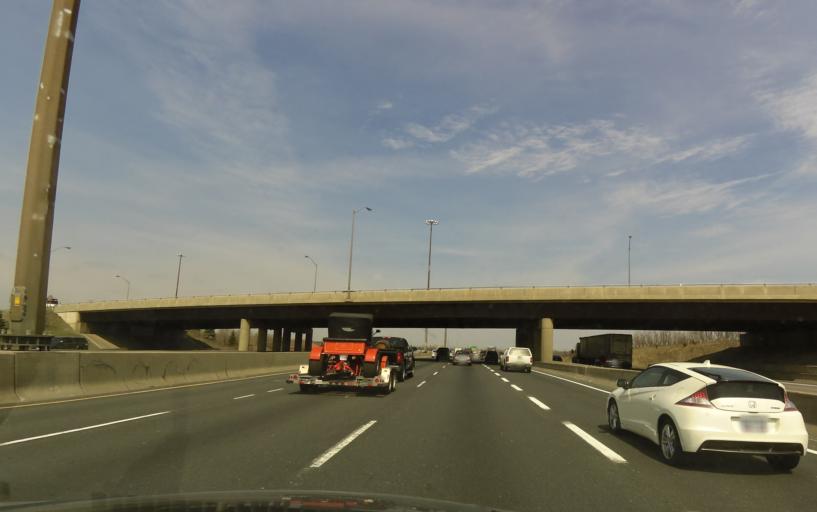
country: CA
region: Ontario
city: Pickering
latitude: 43.8160
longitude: -79.1153
